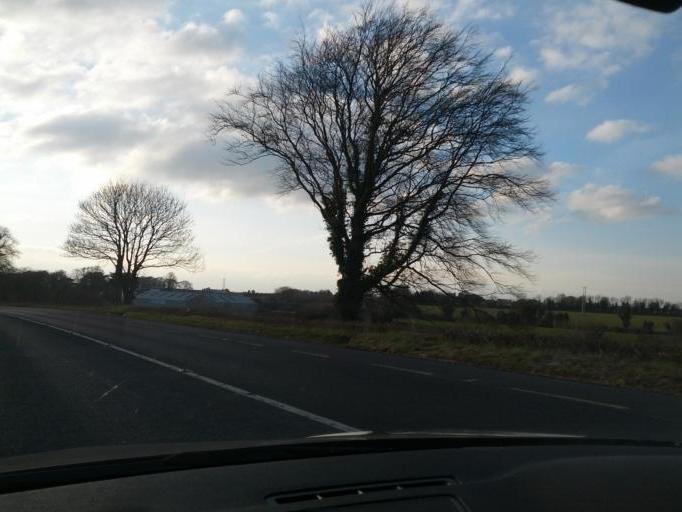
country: IE
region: Munster
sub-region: North Tipperary
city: Nenagh
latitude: 52.8630
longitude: -8.1438
